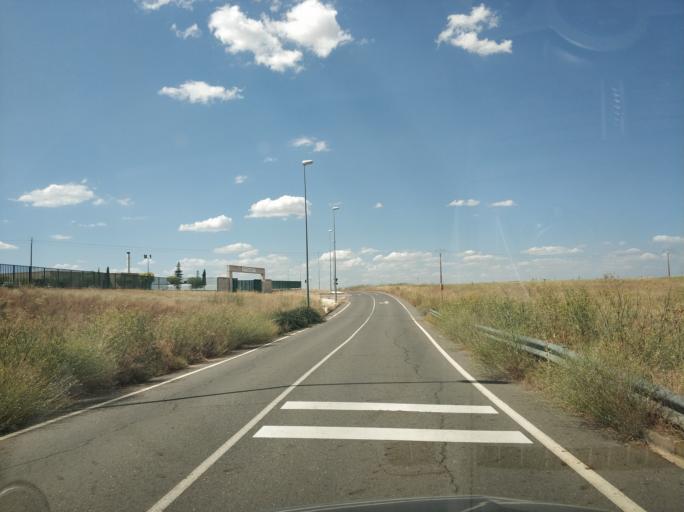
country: ES
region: Castille and Leon
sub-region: Provincia de Salamanca
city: Aldeatejada
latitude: 40.9466
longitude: -5.6932
